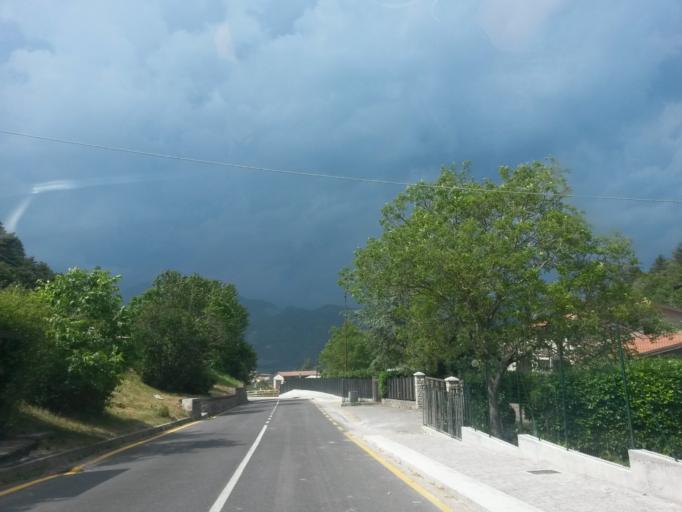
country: IT
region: Lombardy
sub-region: Provincia di Brescia
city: Gardola
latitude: 45.7452
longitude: 10.7322
